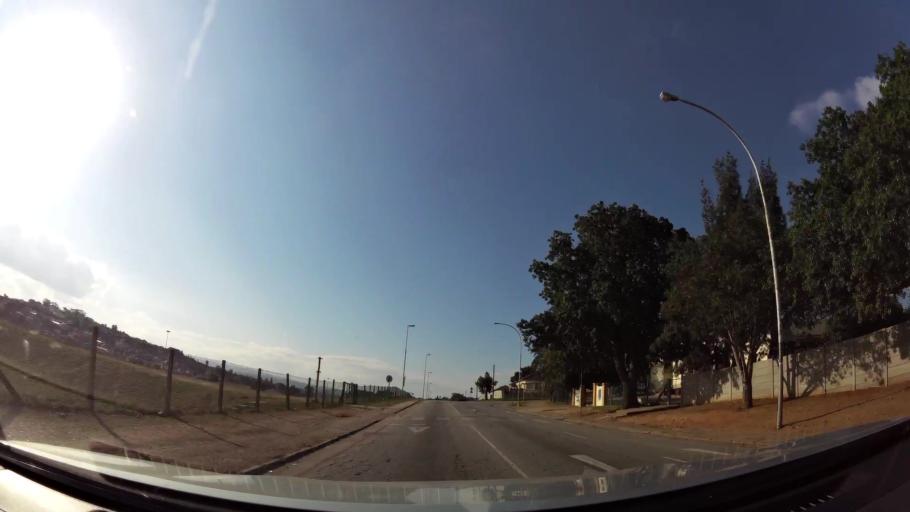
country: ZA
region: Eastern Cape
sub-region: Nelson Mandela Bay Metropolitan Municipality
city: Uitenhage
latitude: -33.7736
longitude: 25.4104
